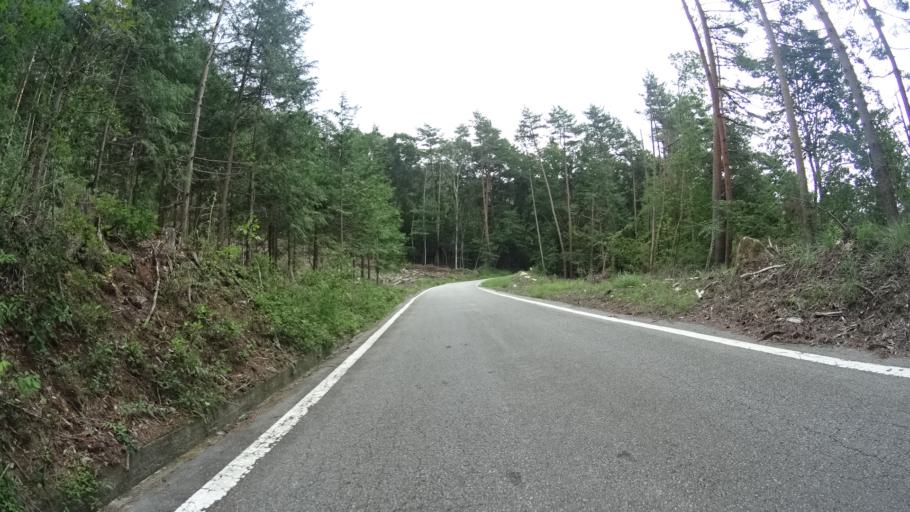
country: JP
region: Yamanashi
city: Kofu-shi
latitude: 35.8048
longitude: 138.5886
